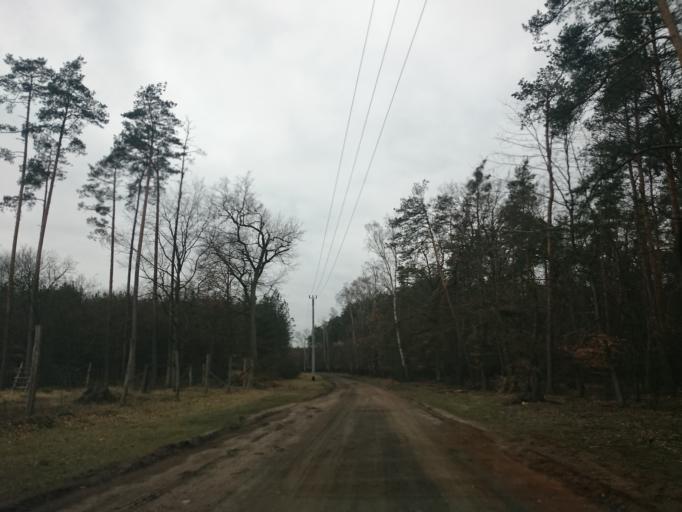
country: PL
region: Kujawsko-Pomorskie
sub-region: Powiat golubsko-dobrzynski
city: Ciechocin
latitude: 53.0752
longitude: 18.9485
